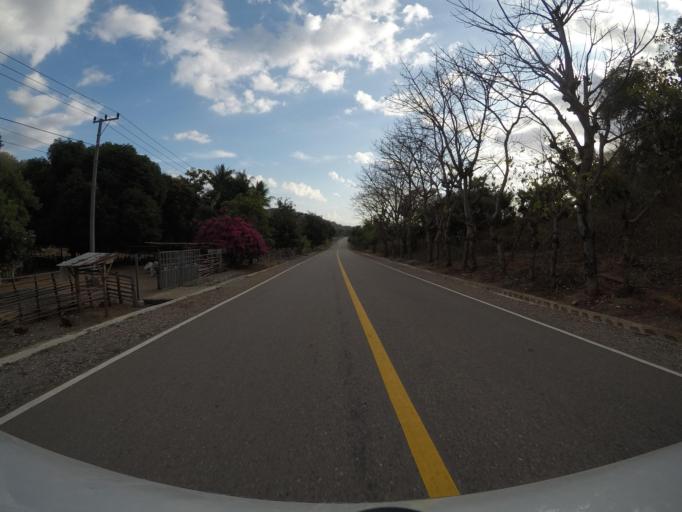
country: TL
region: Bobonaro
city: Maliana
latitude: -8.8747
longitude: 125.0410
